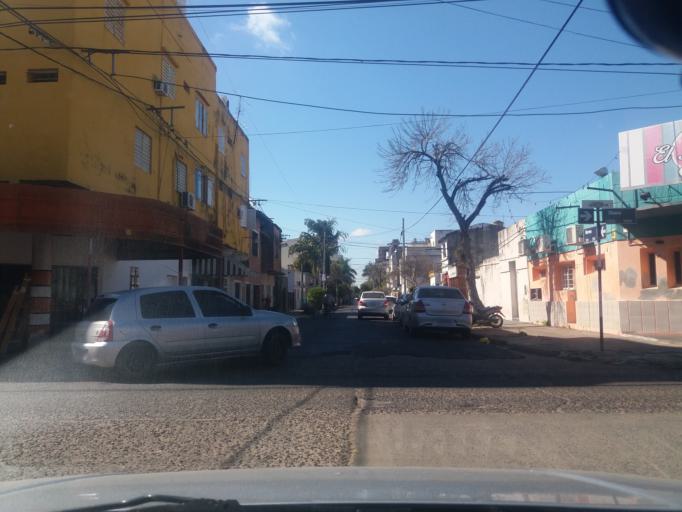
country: AR
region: Corrientes
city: Corrientes
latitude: -27.4724
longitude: -58.8472
